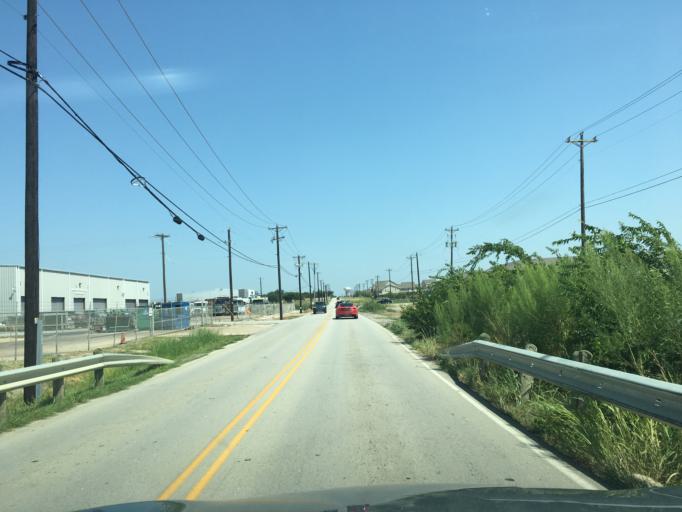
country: US
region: Texas
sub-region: Tarrant County
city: Blue Mound
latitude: 32.9038
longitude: -97.3317
